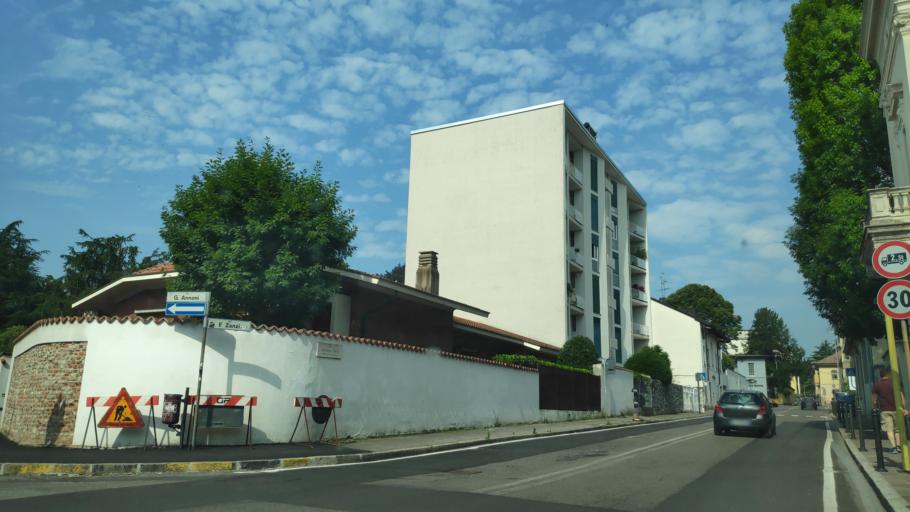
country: IT
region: Lombardy
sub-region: Provincia di Monza e Brianza
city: Monza
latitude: 45.5875
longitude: 9.2800
